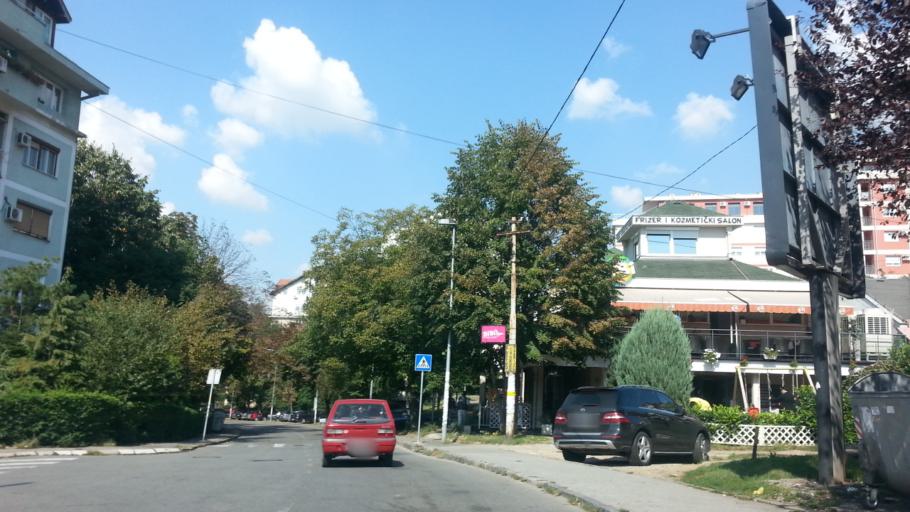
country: RS
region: Central Serbia
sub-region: Belgrade
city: Cukarica
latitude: 44.7719
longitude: 20.4168
